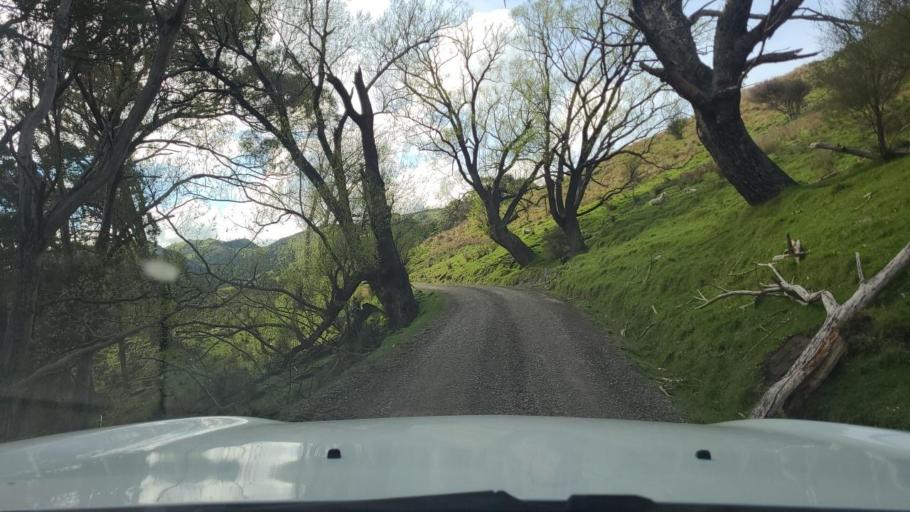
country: NZ
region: Wellington
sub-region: South Wairarapa District
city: Waipawa
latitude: -41.3227
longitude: 175.6512
